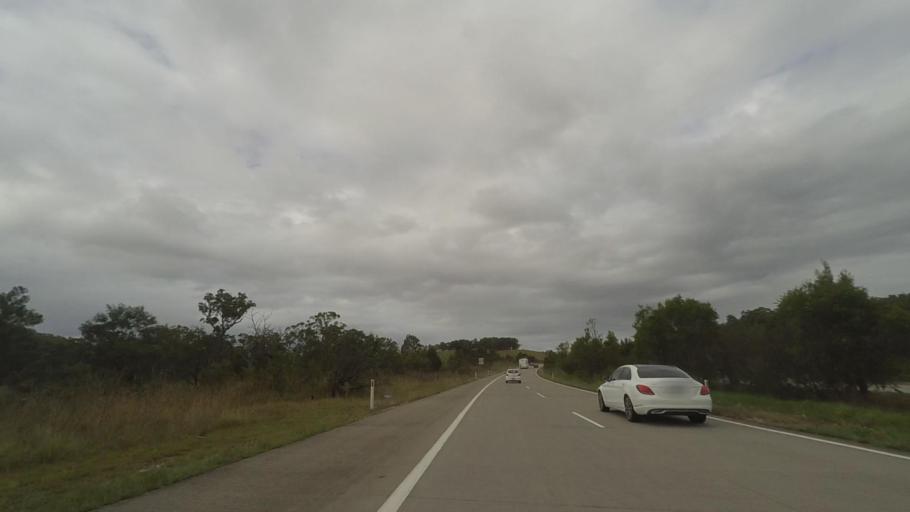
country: AU
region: New South Wales
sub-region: Port Stephens Shire
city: Port Stephens
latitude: -32.6347
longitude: 152.0412
